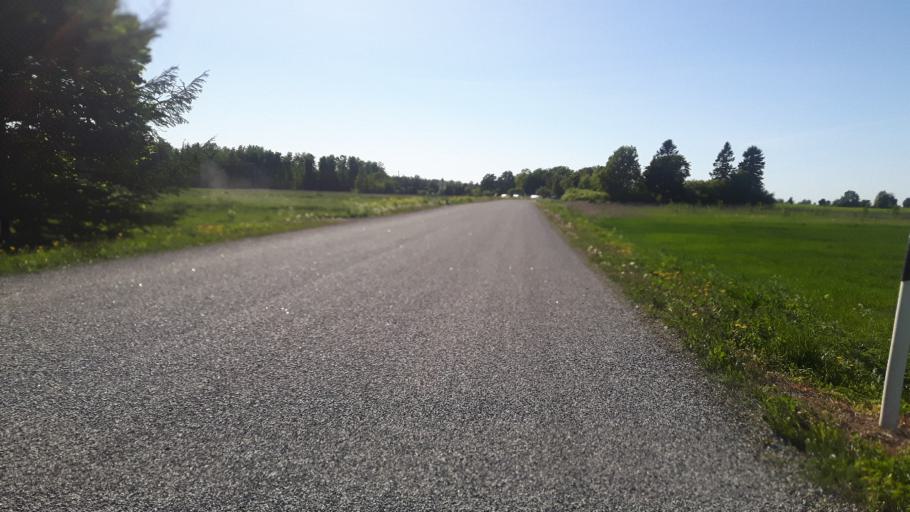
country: EE
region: Ida-Virumaa
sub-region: Kohtla-Jaerve linn
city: Kohtla-Jarve
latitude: 59.4375
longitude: 27.2910
